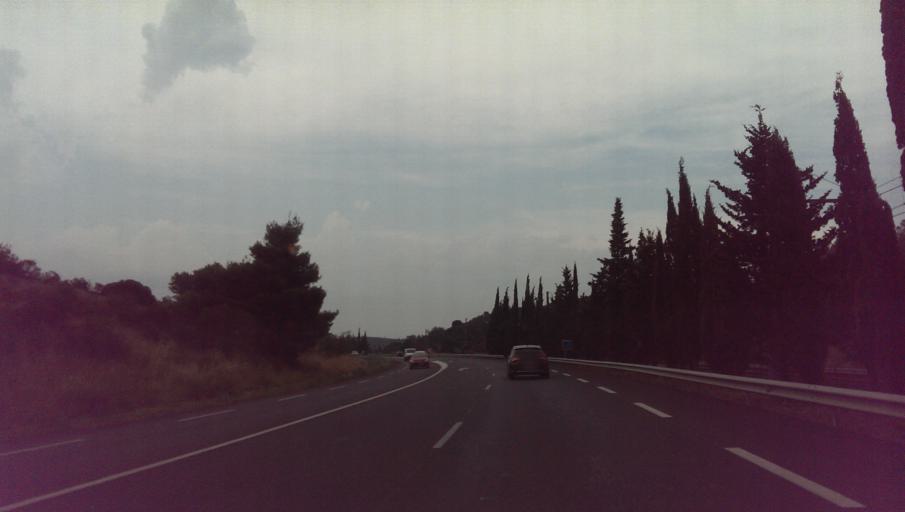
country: FR
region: Languedoc-Roussillon
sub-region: Departement des Pyrenees-Orientales
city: Vinca
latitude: 42.6509
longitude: 2.5393
